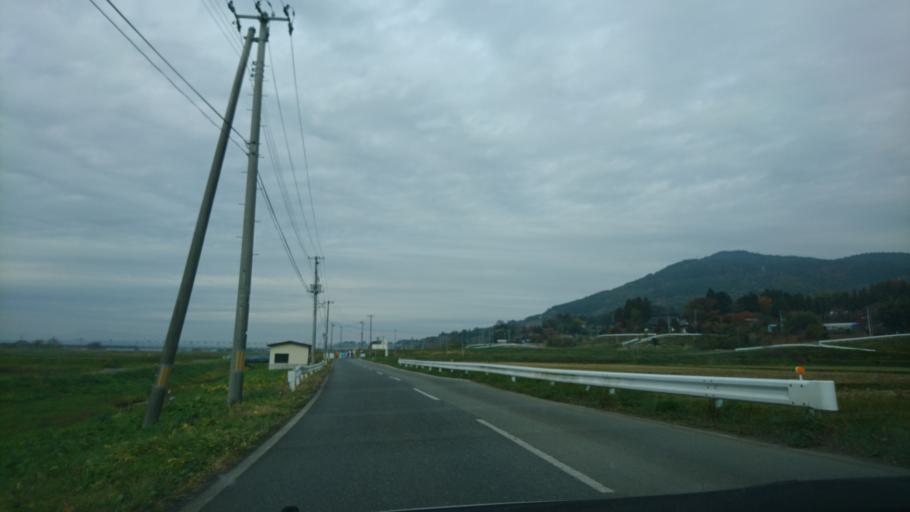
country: JP
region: Iwate
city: Ichinoseki
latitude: 38.9670
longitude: 141.1664
